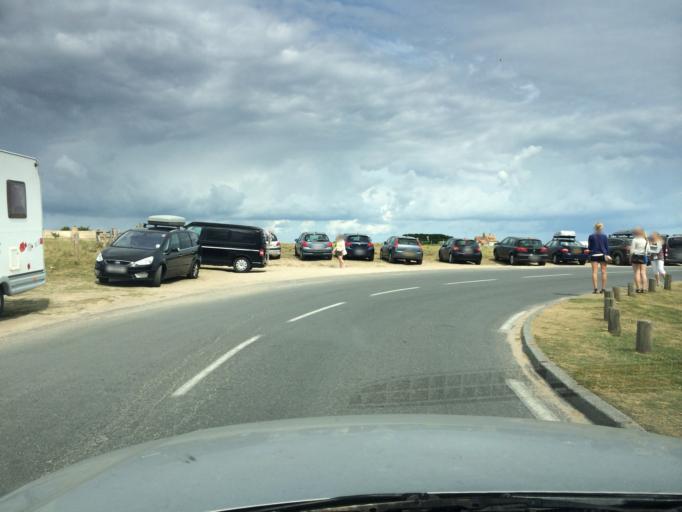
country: FR
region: Lower Normandy
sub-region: Departement de la Manche
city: Saint-Hilaire-Petitville
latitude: 49.4158
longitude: -1.1775
